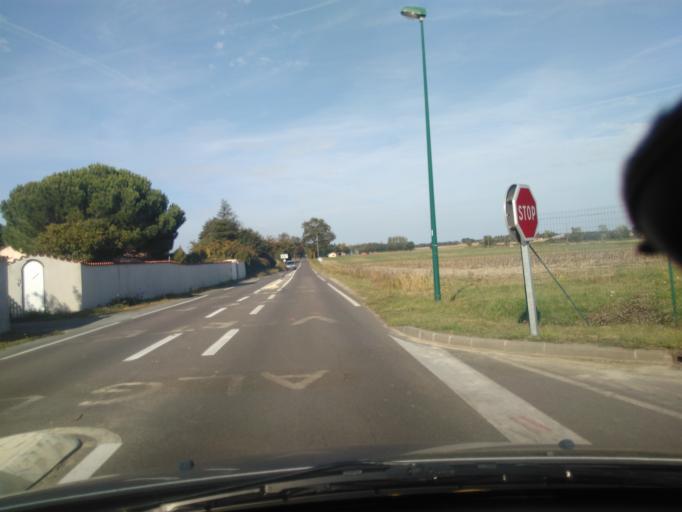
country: FR
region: Pays de la Loire
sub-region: Departement de la Vendee
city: Nieul-le-Dolent
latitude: 46.5250
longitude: -1.5518
